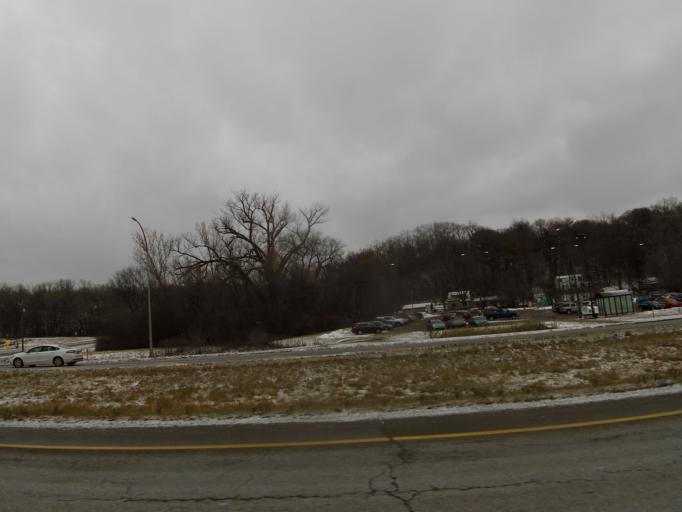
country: US
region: Minnesota
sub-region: Ramsey County
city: Maplewood
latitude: 44.9279
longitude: -93.0225
